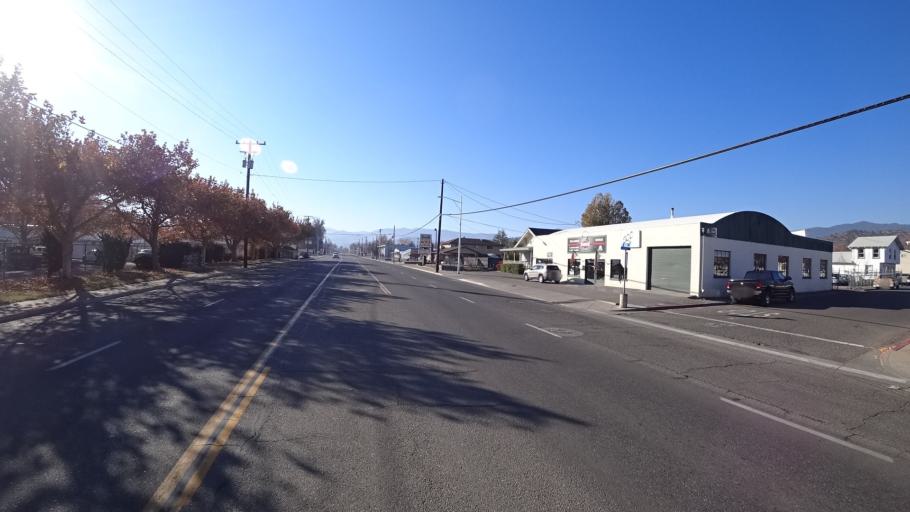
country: US
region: California
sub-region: Siskiyou County
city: Yreka
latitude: 41.7222
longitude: -122.6392
